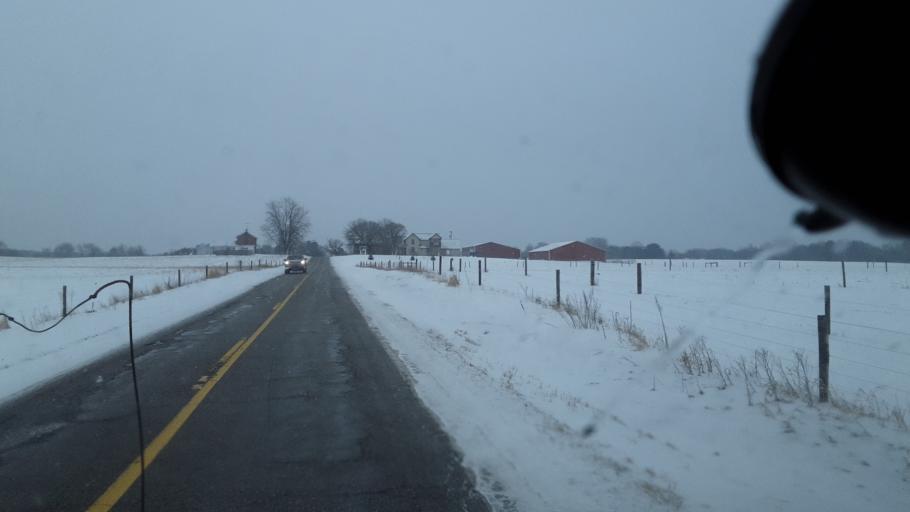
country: US
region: Michigan
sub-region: Ingham County
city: Leslie
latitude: 42.4897
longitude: -84.3237
